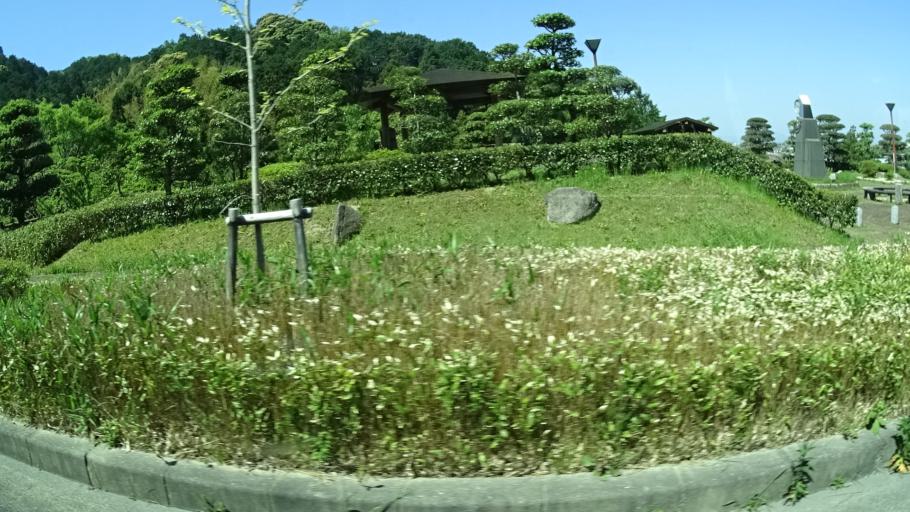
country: JP
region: Mie
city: Toba
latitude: 34.5032
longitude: 136.7810
